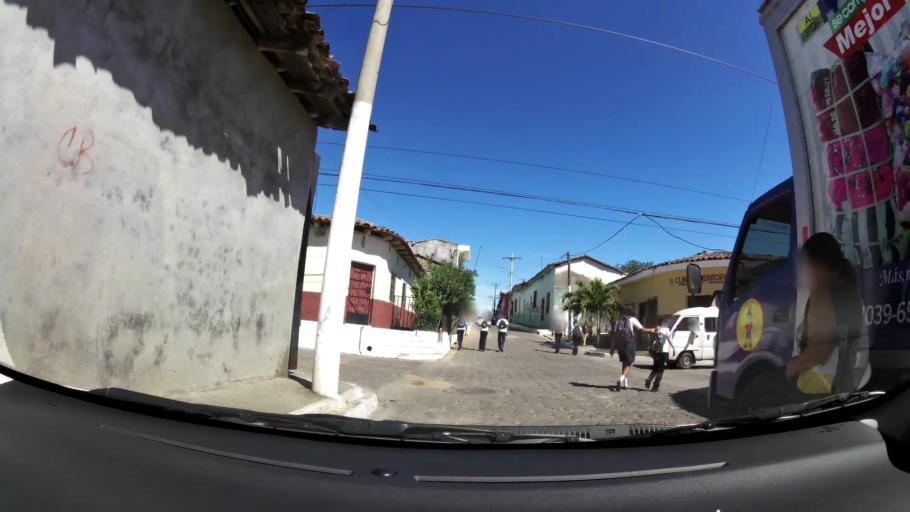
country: SV
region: La Libertad
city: San Juan Opico
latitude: 13.8755
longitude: -89.3595
